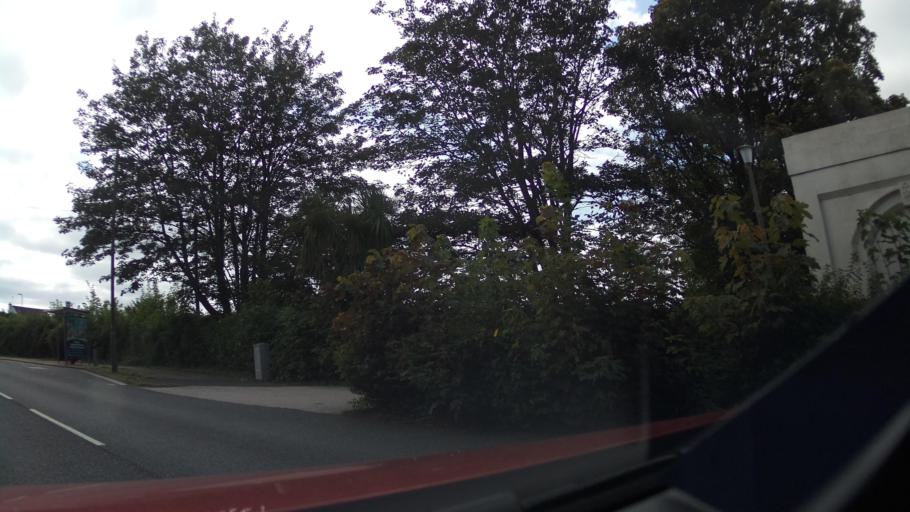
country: GB
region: England
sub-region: Borough of Torbay
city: Torquay
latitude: 50.4910
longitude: -3.5276
